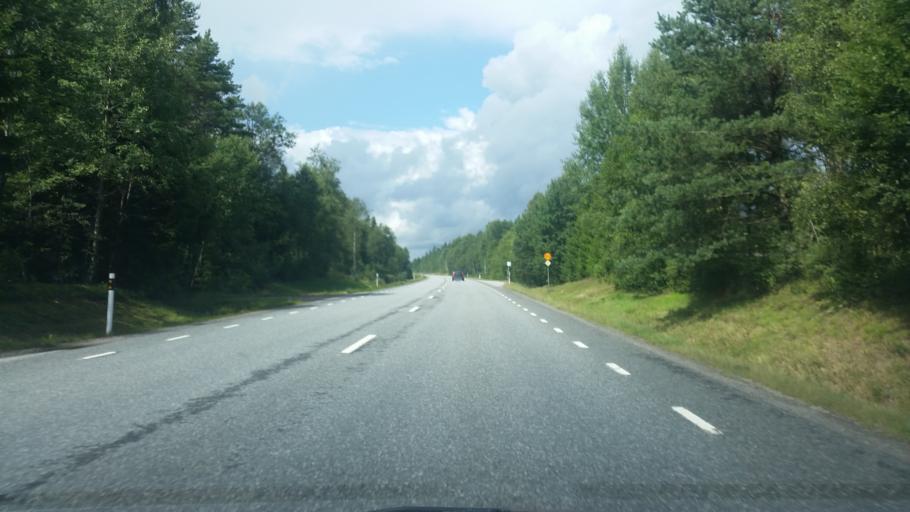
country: SE
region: Vaestra Goetaland
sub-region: Tranemo Kommun
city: Langhem
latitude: 57.5876
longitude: 13.2092
